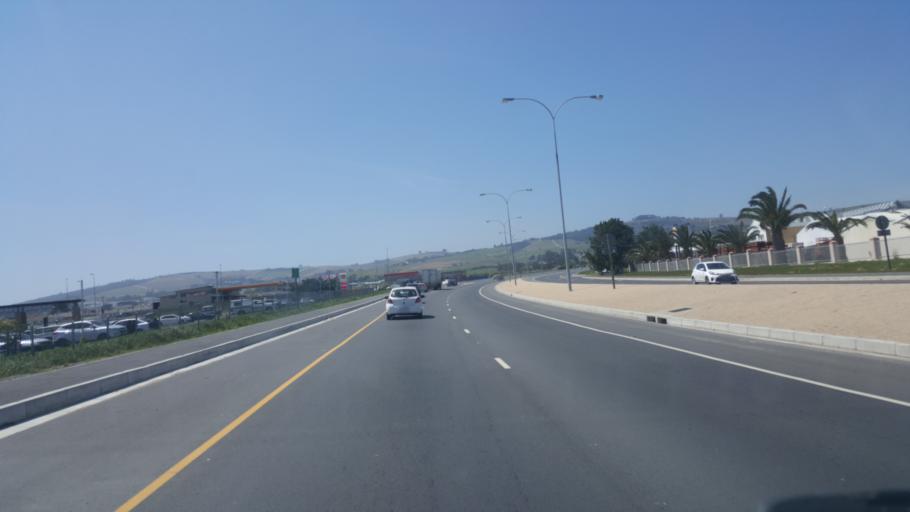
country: ZA
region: Western Cape
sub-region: City of Cape Town
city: Kraaifontein
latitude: -33.9502
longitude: 18.6982
